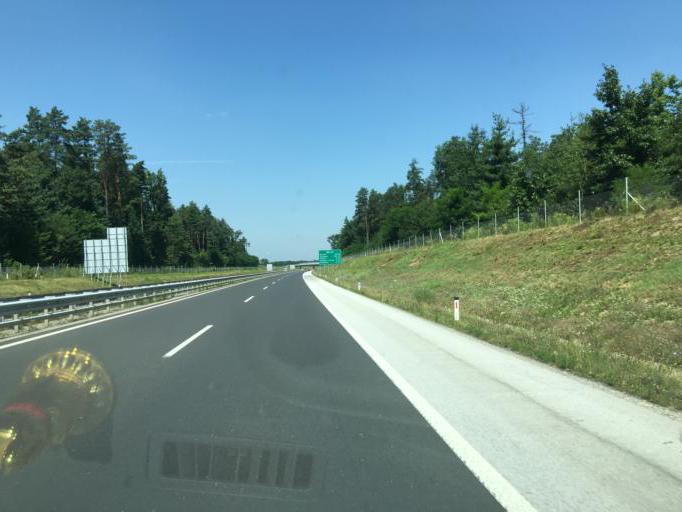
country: SI
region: Kidricevo
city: Kidricevo
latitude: 46.4160
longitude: 15.8063
